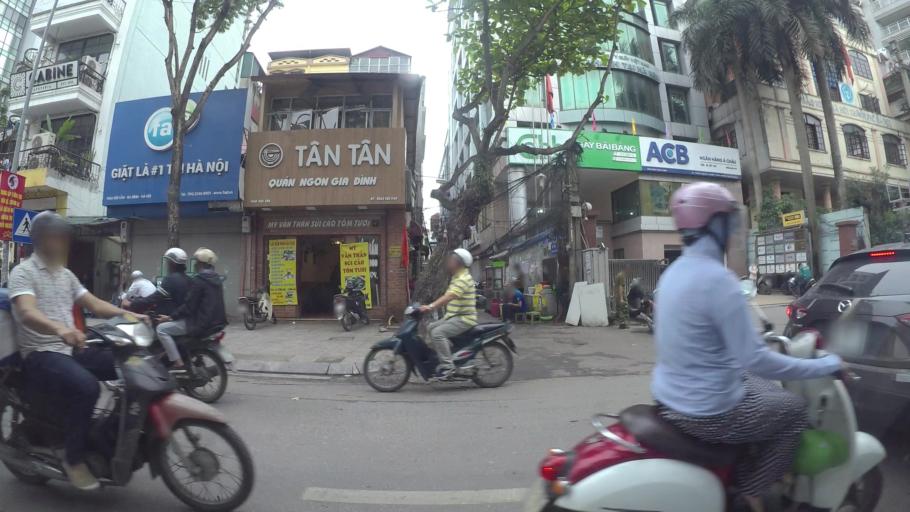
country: VN
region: Ha Noi
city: Dong Da
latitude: 21.0348
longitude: 105.8268
